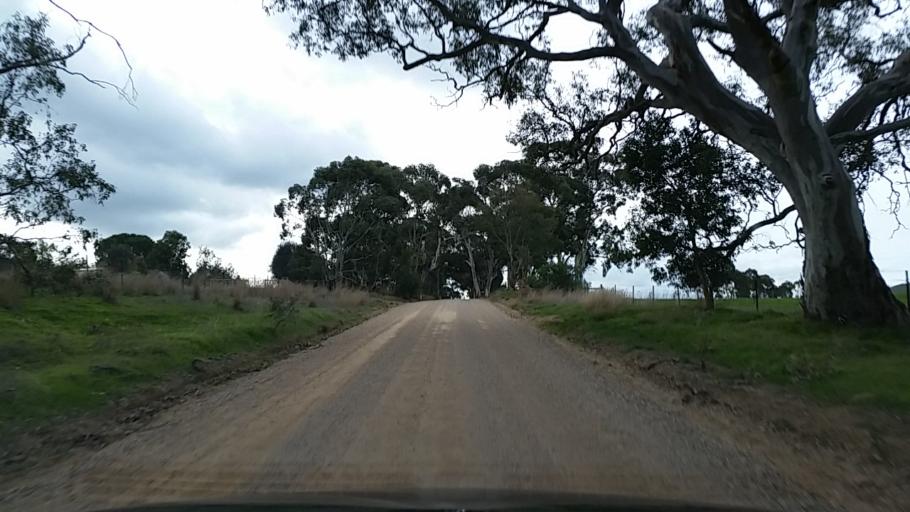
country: AU
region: South Australia
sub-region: Mount Barker
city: Nairne
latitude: -34.9643
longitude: 139.0238
